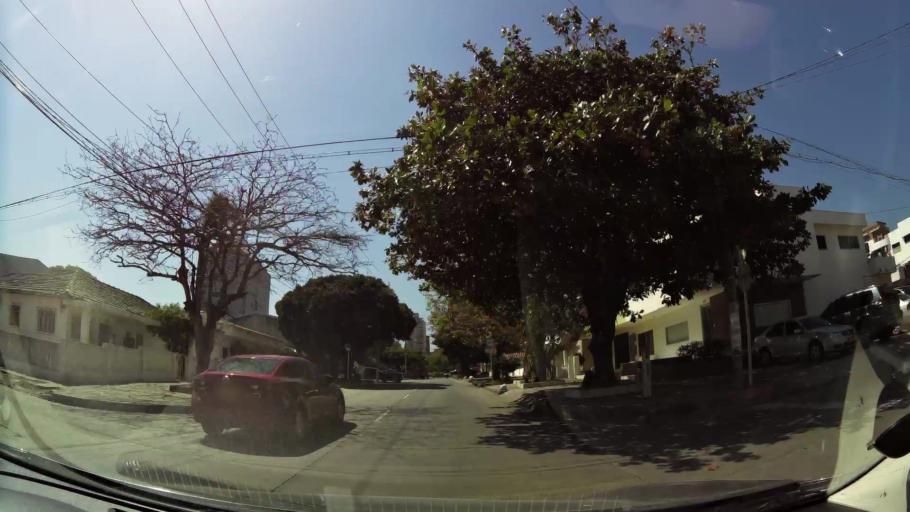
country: CO
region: Atlantico
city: Barranquilla
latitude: 11.0124
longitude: -74.8063
